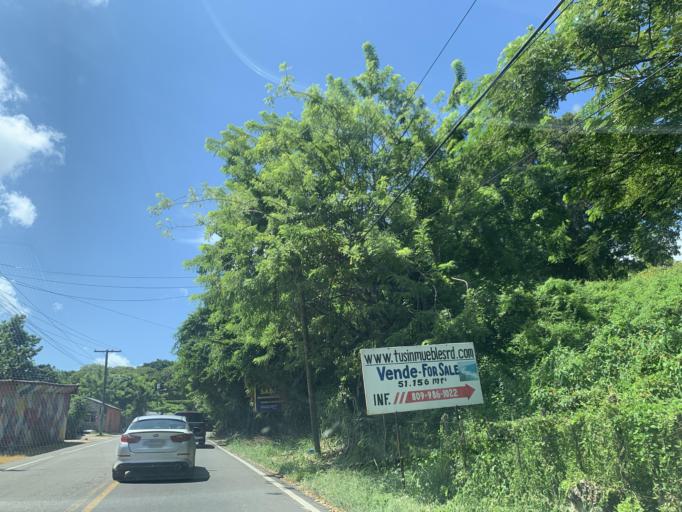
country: DO
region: Maria Trinidad Sanchez
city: Cabrera
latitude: 19.6510
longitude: -69.9315
